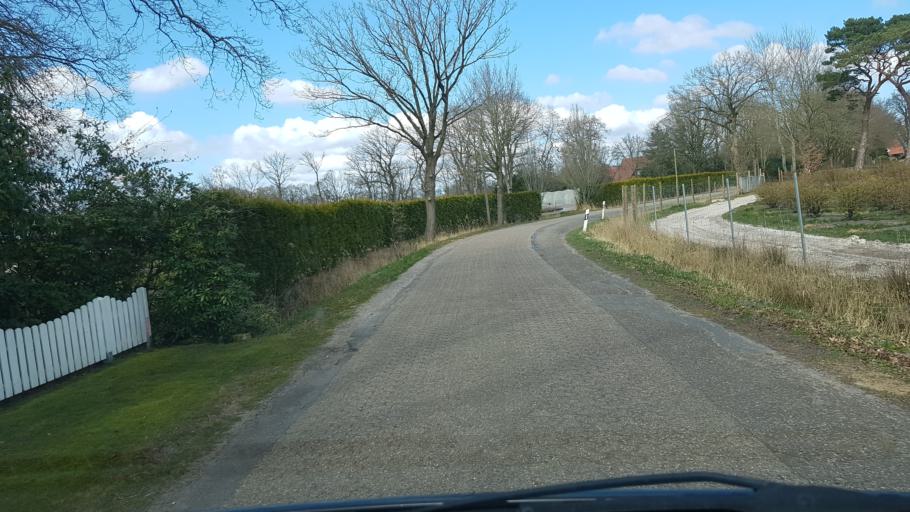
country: DE
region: Lower Saxony
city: Edewecht
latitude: 53.1601
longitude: 7.9365
